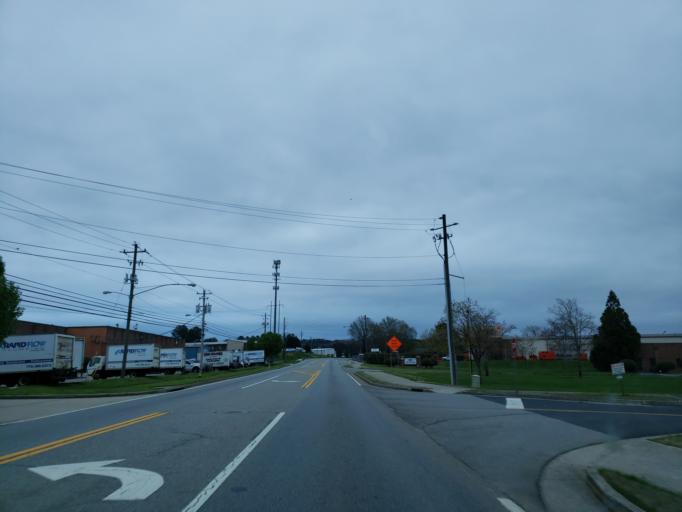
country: US
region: Georgia
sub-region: Bartow County
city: Cartersville
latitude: 34.1504
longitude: -84.8225
